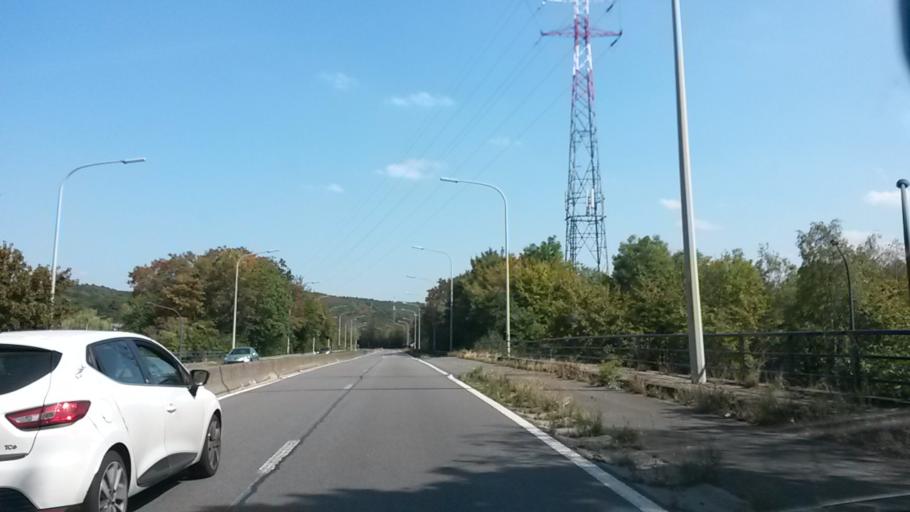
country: BE
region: Wallonia
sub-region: Province du Hainaut
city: Aiseau
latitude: 50.4499
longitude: 4.6044
